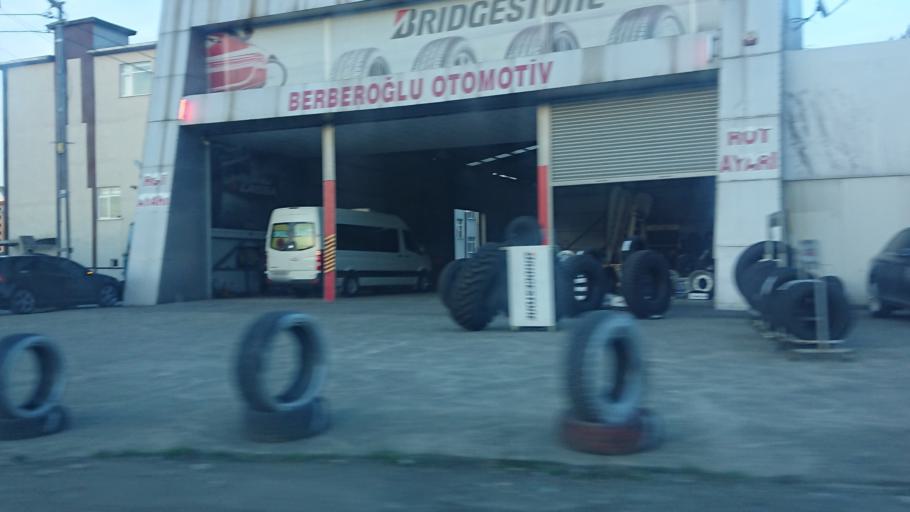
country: TR
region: Rize
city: Gundogdu
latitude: 41.0392
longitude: 40.5795
